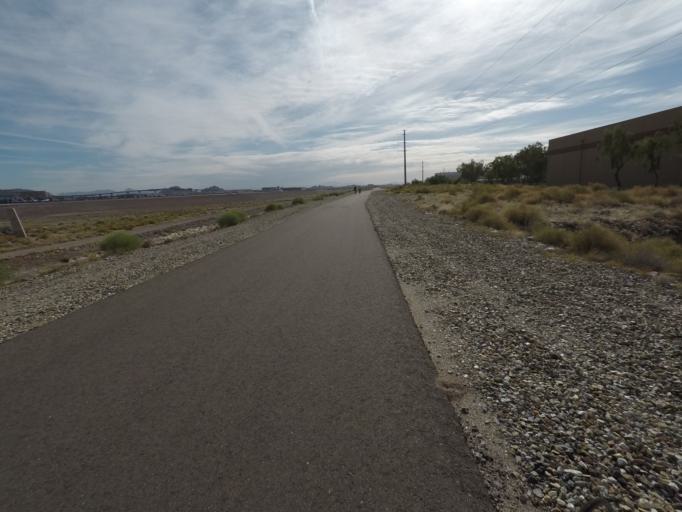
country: US
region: Arizona
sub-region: Maricopa County
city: Tempe Junction
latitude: 33.4250
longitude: -112.0024
